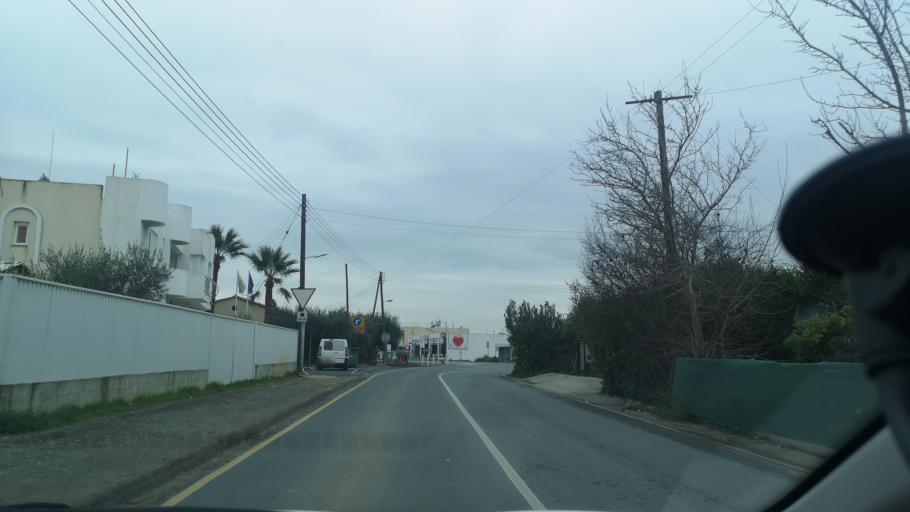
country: CY
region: Lefkosia
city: Kato Deftera
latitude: 35.0867
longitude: 33.2829
